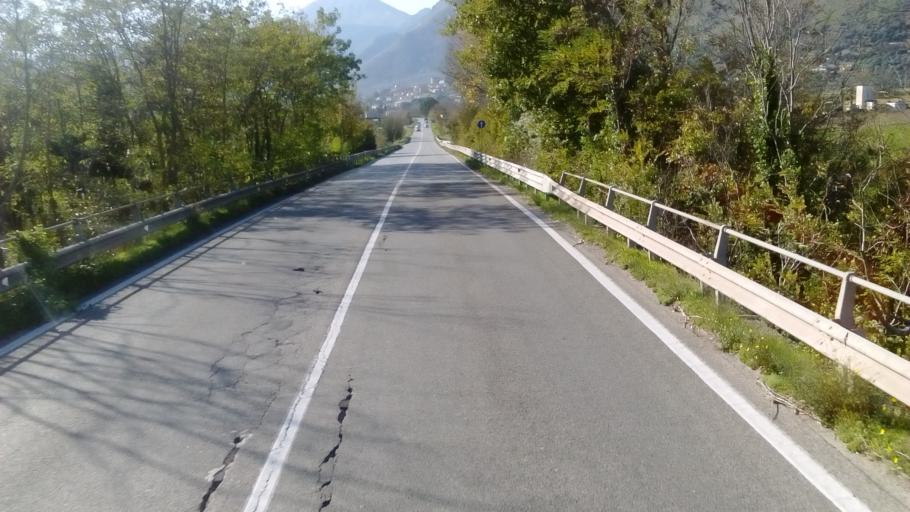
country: IT
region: Molise
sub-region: Provincia di Isernia
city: Pozzilli
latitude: 41.4935
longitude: 14.0690
